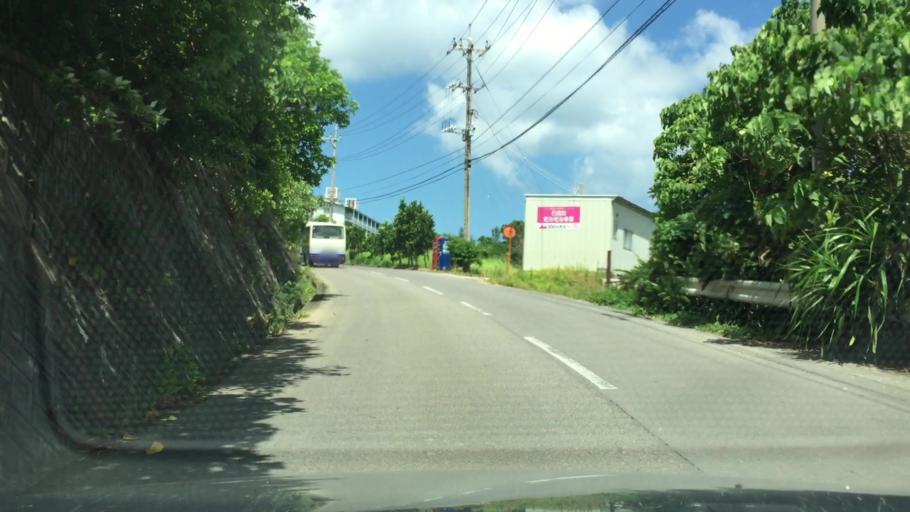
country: JP
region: Okinawa
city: Ishigaki
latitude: 24.3772
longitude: 124.1247
